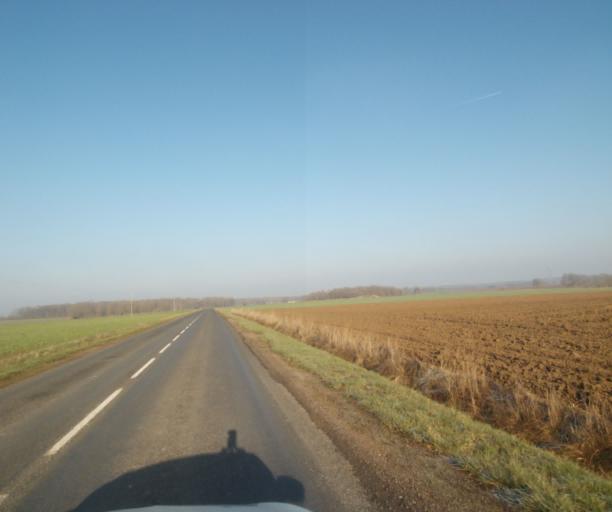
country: FR
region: Champagne-Ardenne
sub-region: Departement de la Haute-Marne
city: Montier-en-Der
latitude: 48.4980
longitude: 4.7525
